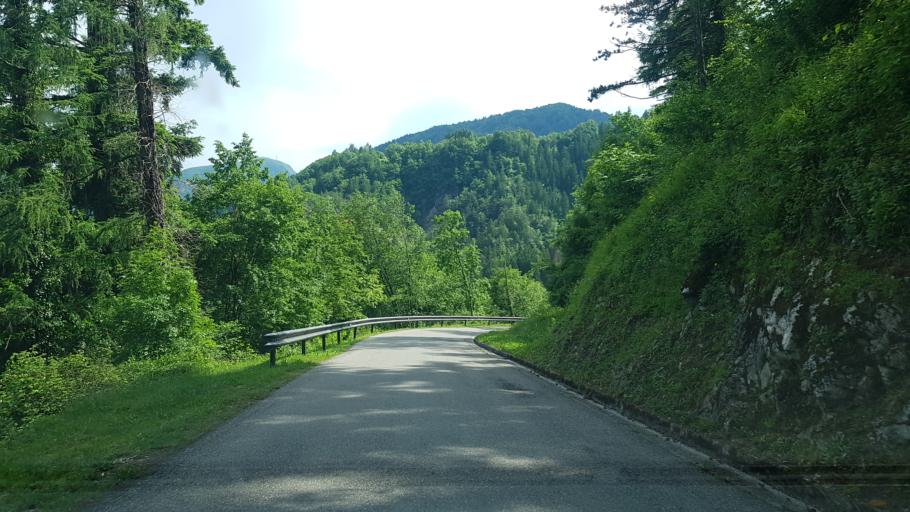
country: IT
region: Friuli Venezia Giulia
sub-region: Provincia di Udine
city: Zuglio
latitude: 46.4666
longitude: 13.0202
